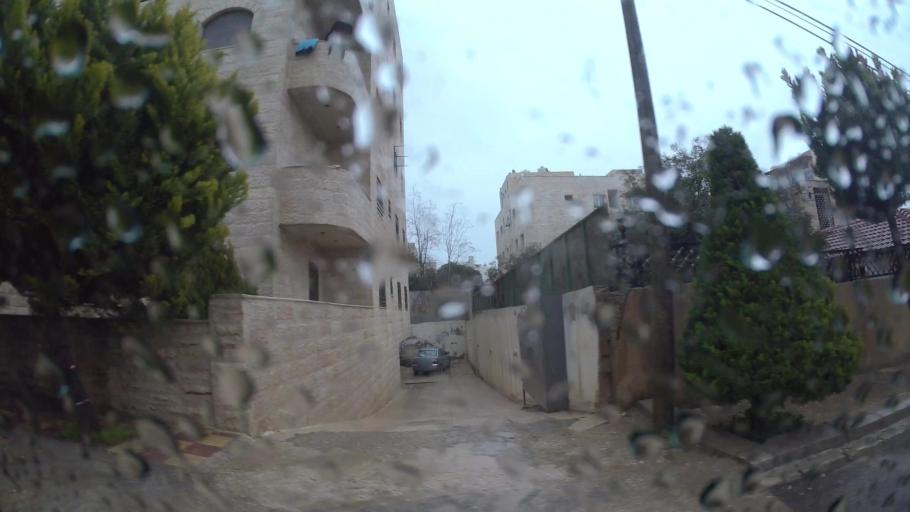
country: JO
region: Amman
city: Al Jubayhah
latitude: 32.0410
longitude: 35.8922
